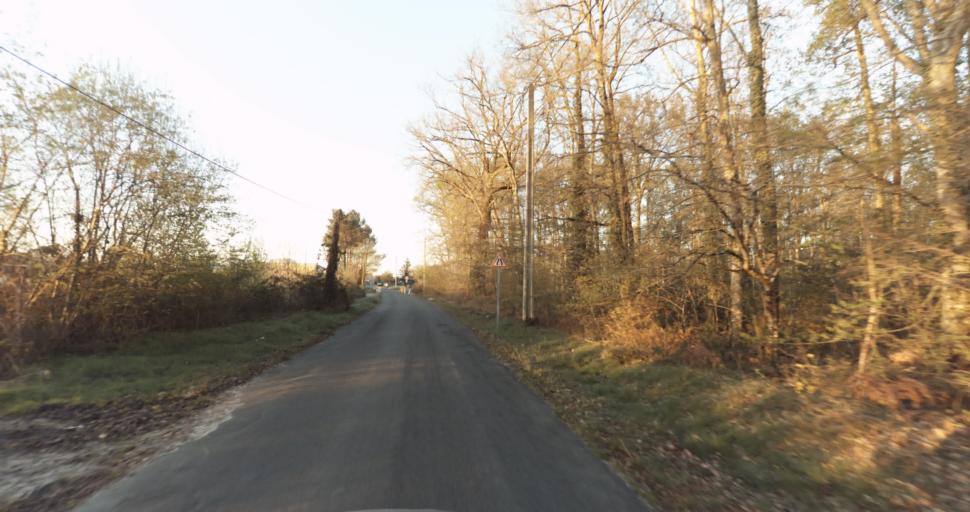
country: FR
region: Aquitaine
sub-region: Departement de la Gironde
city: Martignas-sur-Jalle
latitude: 44.8179
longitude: -0.7440
